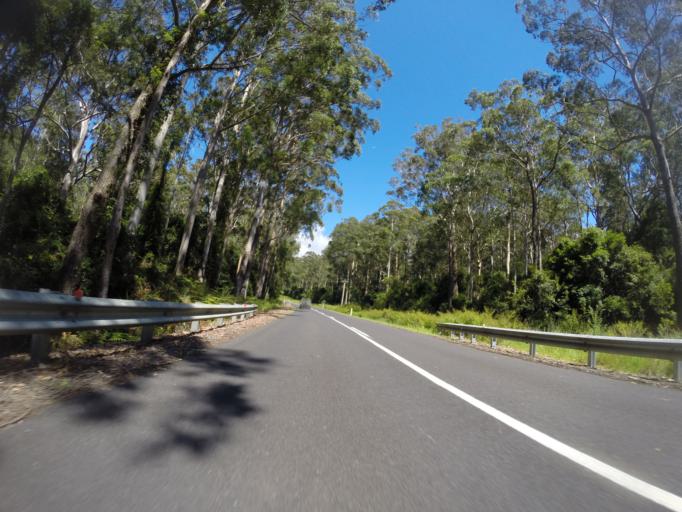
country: AU
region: New South Wales
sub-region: Eurobodalla
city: Batemans Bay
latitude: -35.6571
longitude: 150.2717
